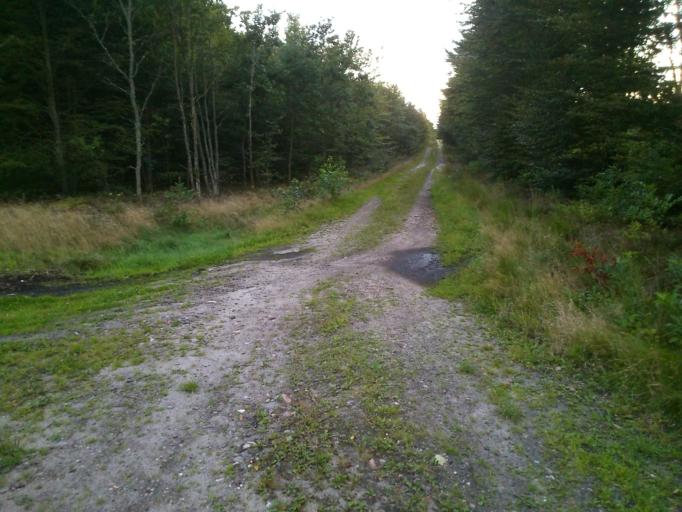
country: DK
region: Central Jutland
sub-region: Ringkobing-Skjern Kommune
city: Skjern
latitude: 56.0105
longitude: 8.4577
